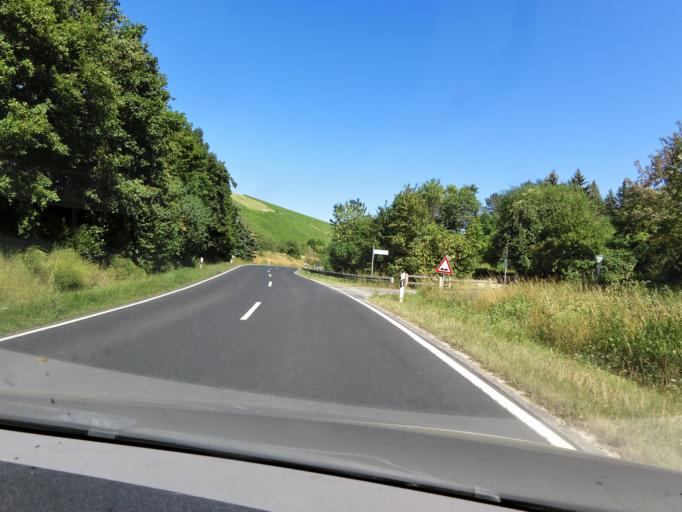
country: DE
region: Bavaria
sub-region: Regierungsbezirk Unterfranken
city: Randersacker
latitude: 49.7554
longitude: 9.9965
